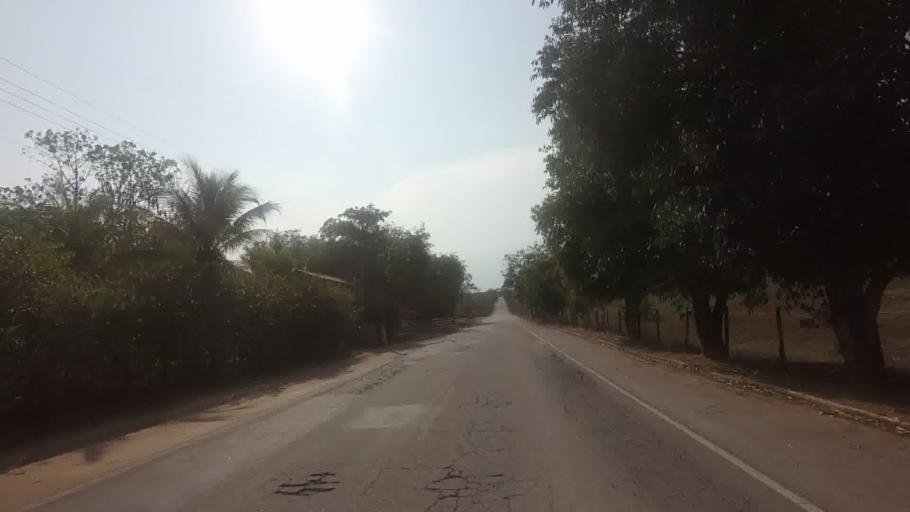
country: BR
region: Rio de Janeiro
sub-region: Bom Jesus Do Itabapoana
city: Bom Jesus do Itabapoana
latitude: -21.1437
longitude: -41.6270
